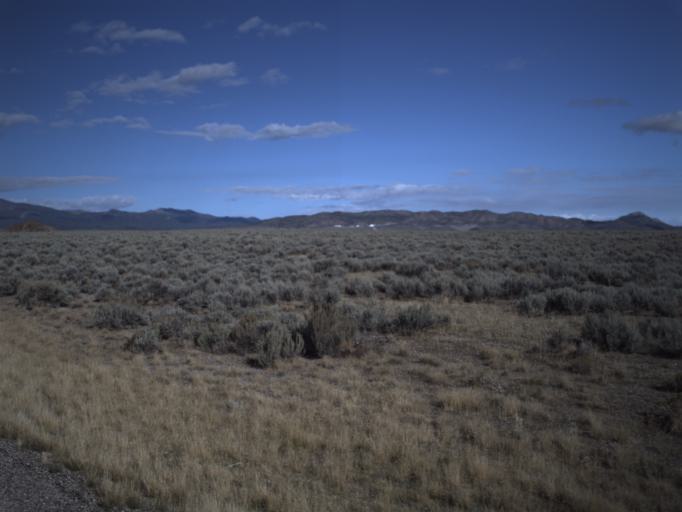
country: US
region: Utah
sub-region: Beaver County
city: Milford
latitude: 38.4148
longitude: -113.0787
